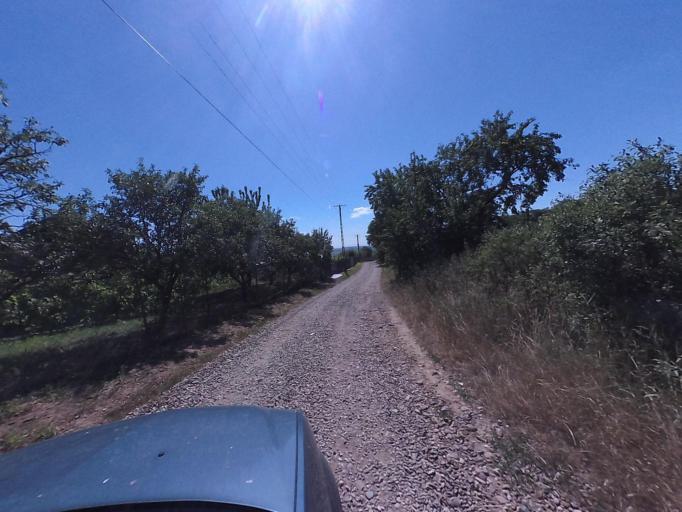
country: RO
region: Vaslui
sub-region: Comuna Costesti
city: Costesti
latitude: 46.4779
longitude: 27.7937
